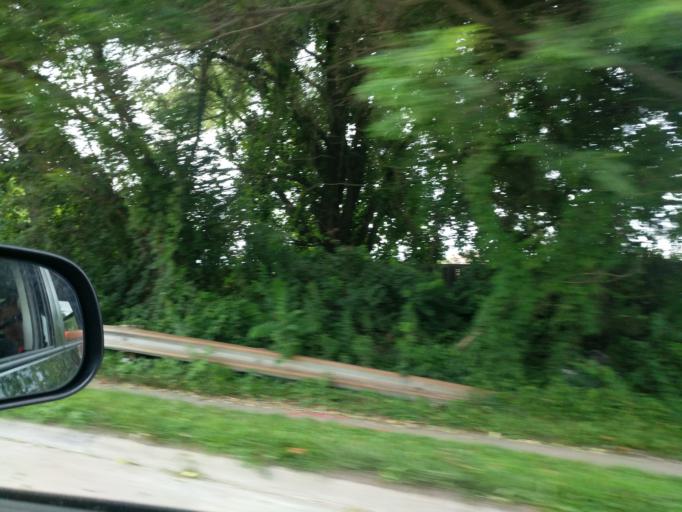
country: US
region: New York
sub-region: Nassau County
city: Barnum Island
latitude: 40.6207
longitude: -73.6479
